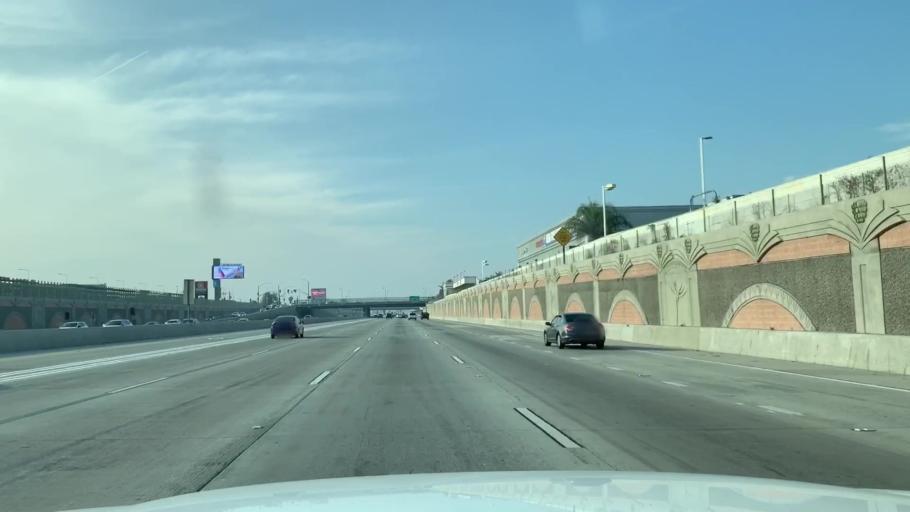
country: US
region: California
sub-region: Orange County
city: Buena Park
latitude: 33.8647
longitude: -117.9945
